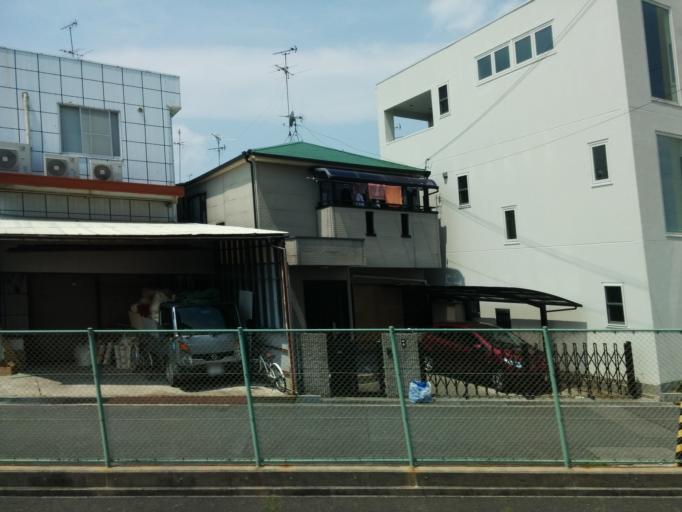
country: JP
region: Osaka
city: Ibaraki
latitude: 34.7933
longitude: 135.5587
